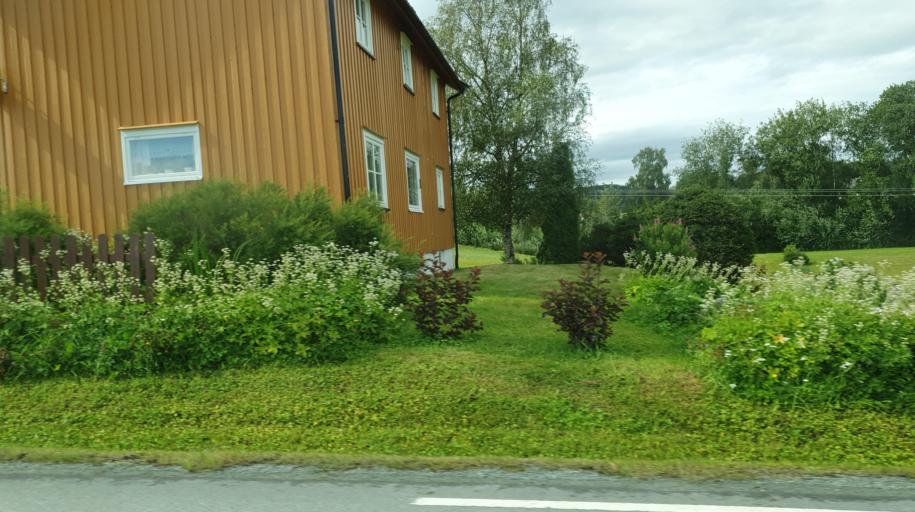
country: NO
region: Nord-Trondelag
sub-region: Stjordal
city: Stjordalshalsen
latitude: 63.5107
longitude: 11.0811
